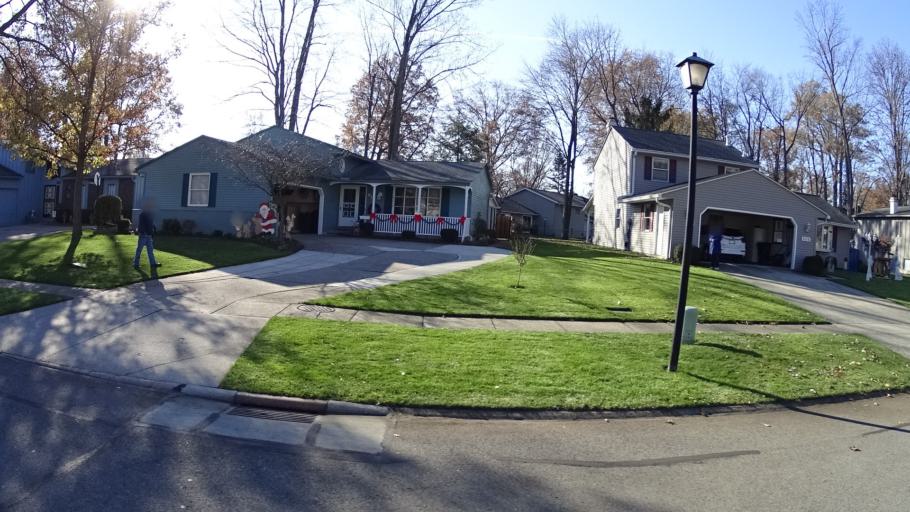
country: US
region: Ohio
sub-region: Lorain County
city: Sheffield
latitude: 41.3921
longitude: -82.0710
